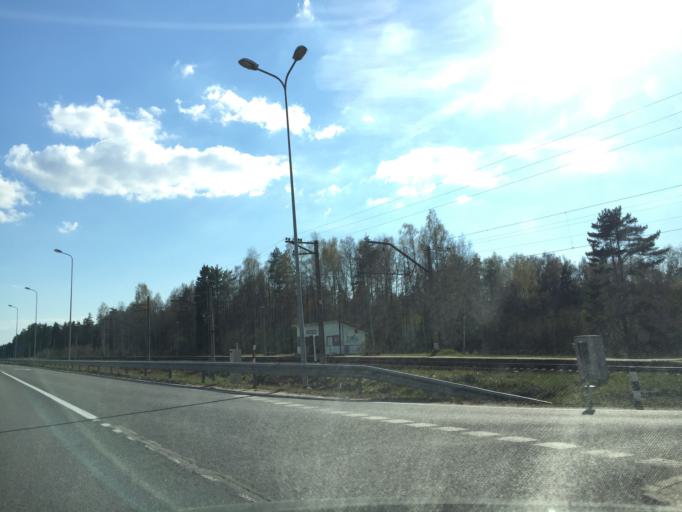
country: LV
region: Saulkrastu
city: Saulkrasti
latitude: 57.3075
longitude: 24.4434
